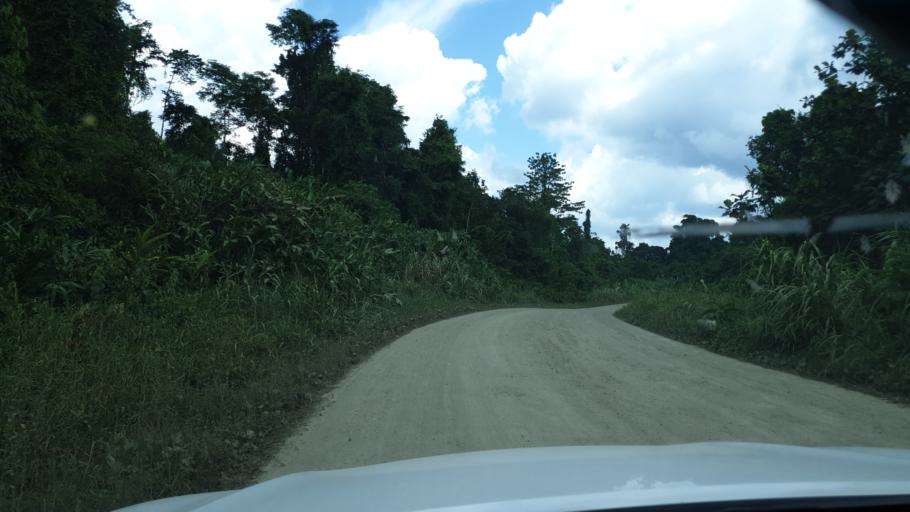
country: PG
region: East Sepik
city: Angoram
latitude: -3.8970
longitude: 143.9199
